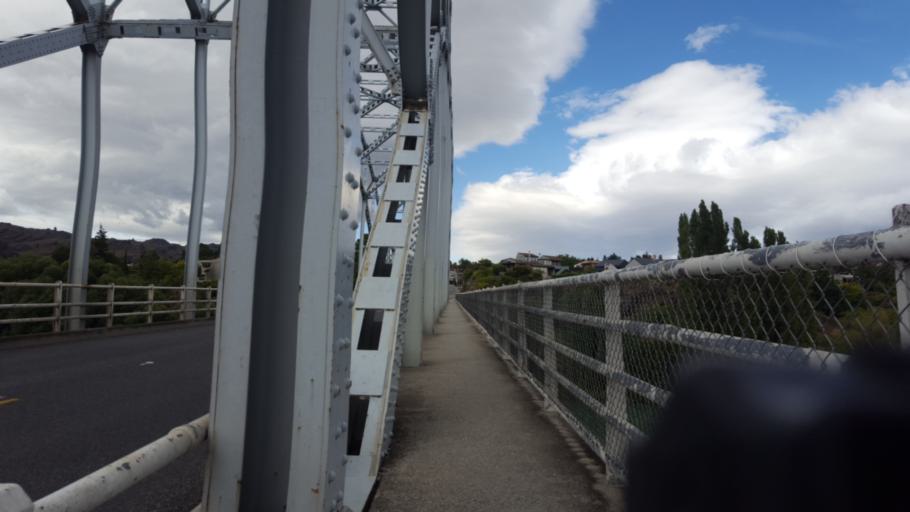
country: NZ
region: Otago
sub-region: Queenstown-Lakes District
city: Wanaka
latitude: -45.2581
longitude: 169.3909
